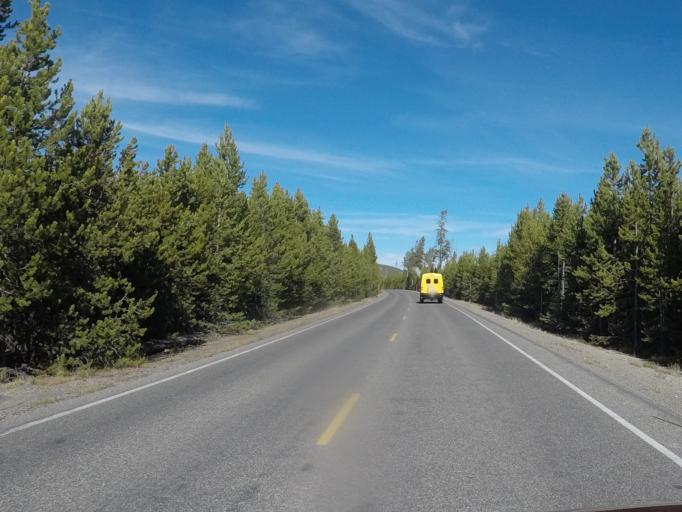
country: US
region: Montana
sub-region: Gallatin County
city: West Yellowstone
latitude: 44.4753
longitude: -110.8559
